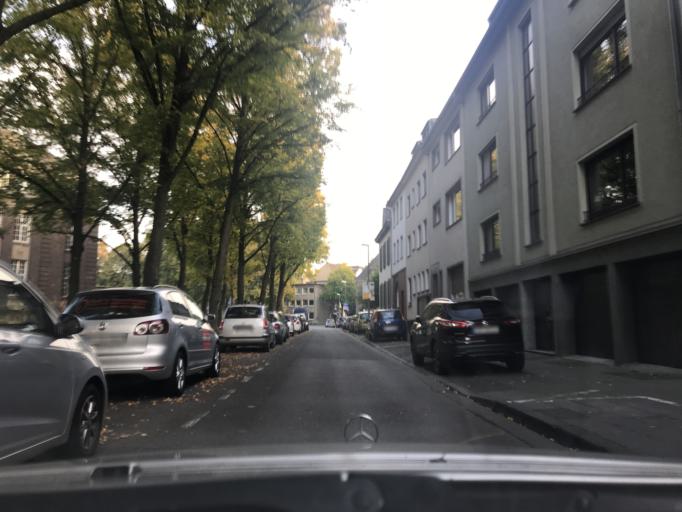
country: DE
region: North Rhine-Westphalia
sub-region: Regierungsbezirk Dusseldorf
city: Krefeld
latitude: 51.3390
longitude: 6.5772
